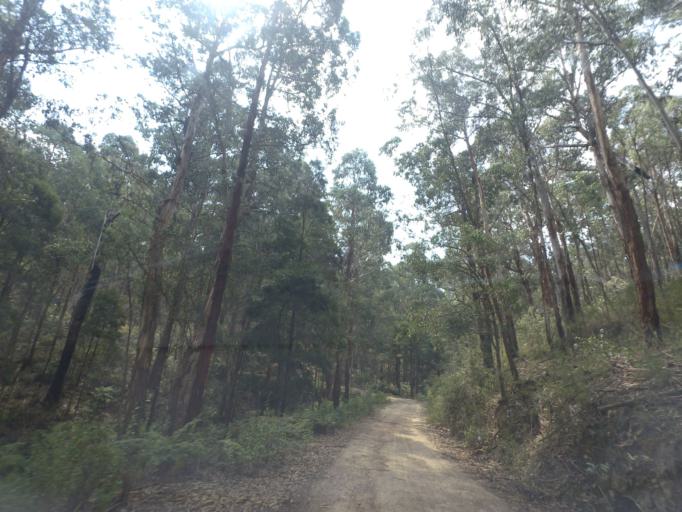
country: AU
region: Victoria
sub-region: Moorabool
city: Bacchus Marsh
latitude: -37.4644
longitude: 144.3913
